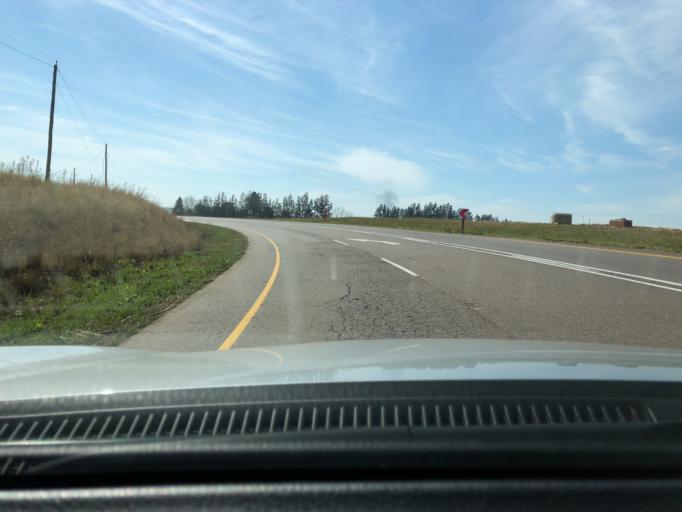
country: ZA
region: KwaZulu-Natal
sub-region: uMgungundlovu District Municipality
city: Richmond
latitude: -29.7953
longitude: 30.3487
